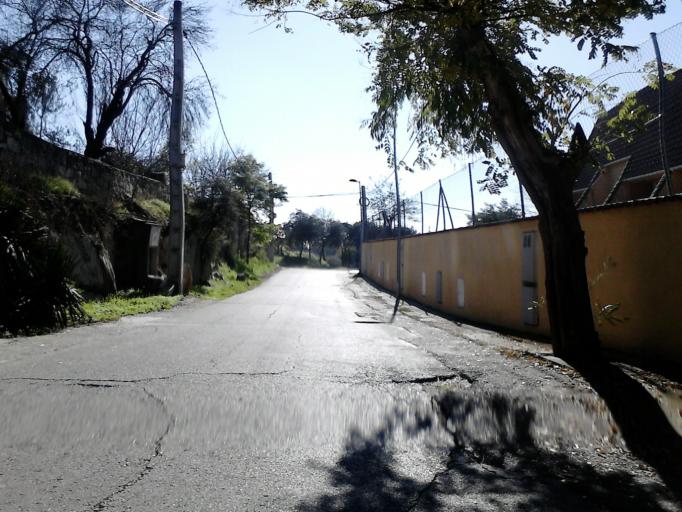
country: ES
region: Madrid
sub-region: Provincia de Madrid
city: Torrelodones
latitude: 40.5851
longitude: -3.9646
